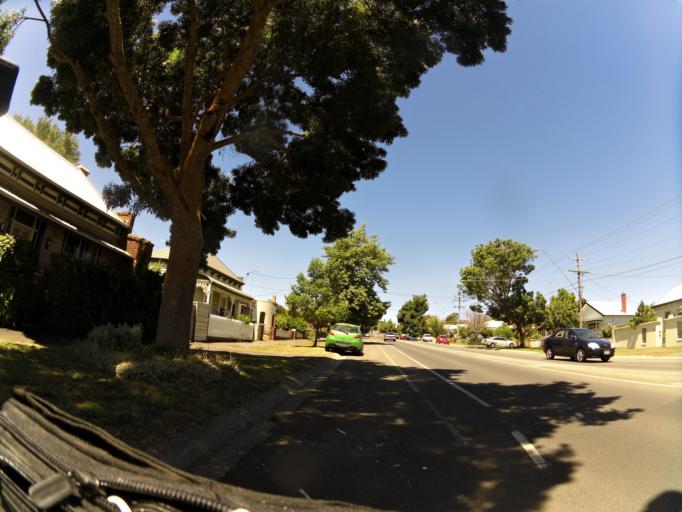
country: AU
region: Victoria
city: Ballarat East
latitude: -37.5687
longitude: 143.8611
